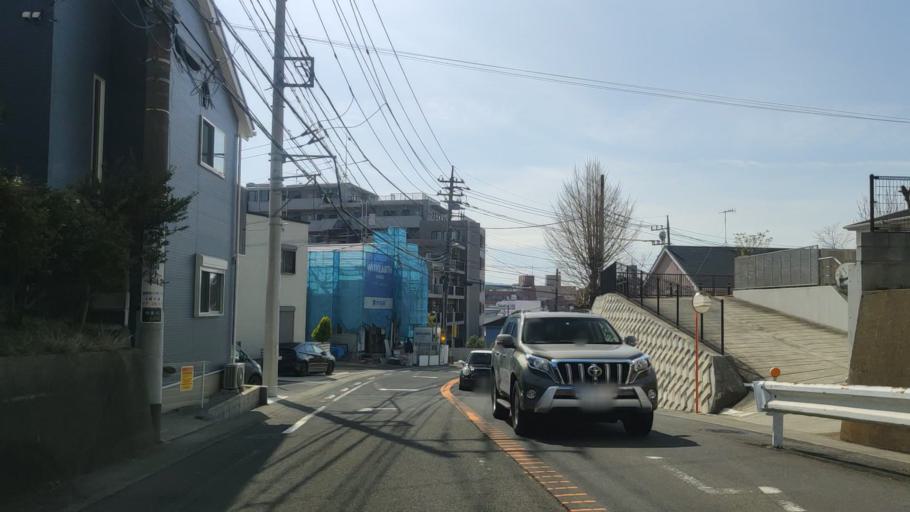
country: JP
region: Kanagawa
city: Isehara
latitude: 35.3857
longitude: 139.2803
